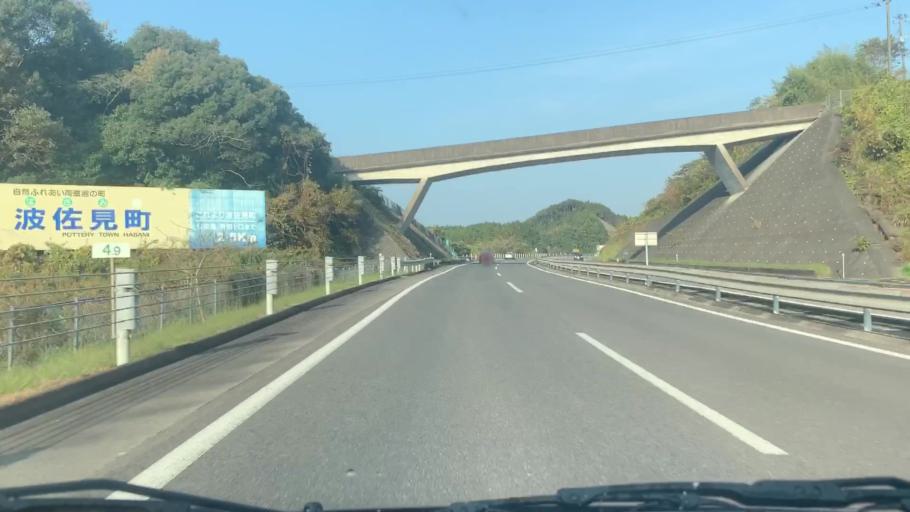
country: JP
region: Saga Prefecture
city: Ureshinomachi-shimojuku
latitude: 33.1488
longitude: 129.9390
